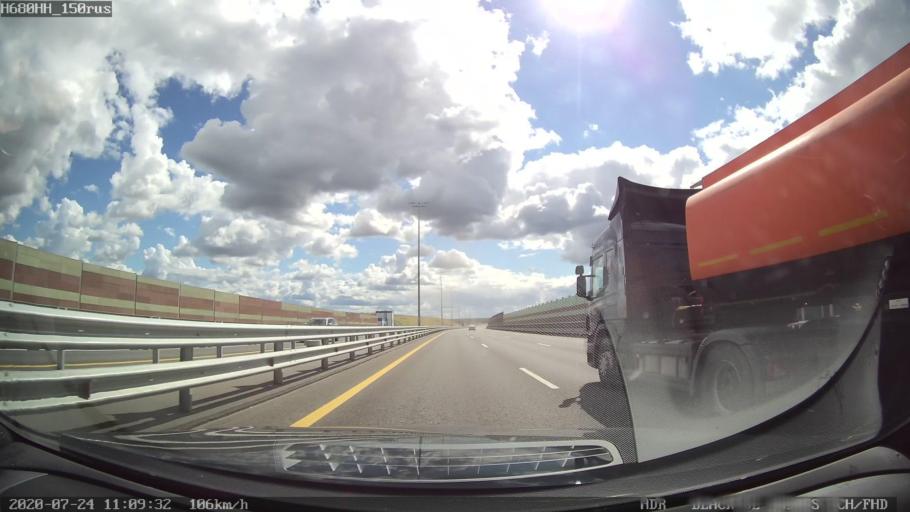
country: RU
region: St.-Petersburg
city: Tyarlevo
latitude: 59.7483
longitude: 30.4776
